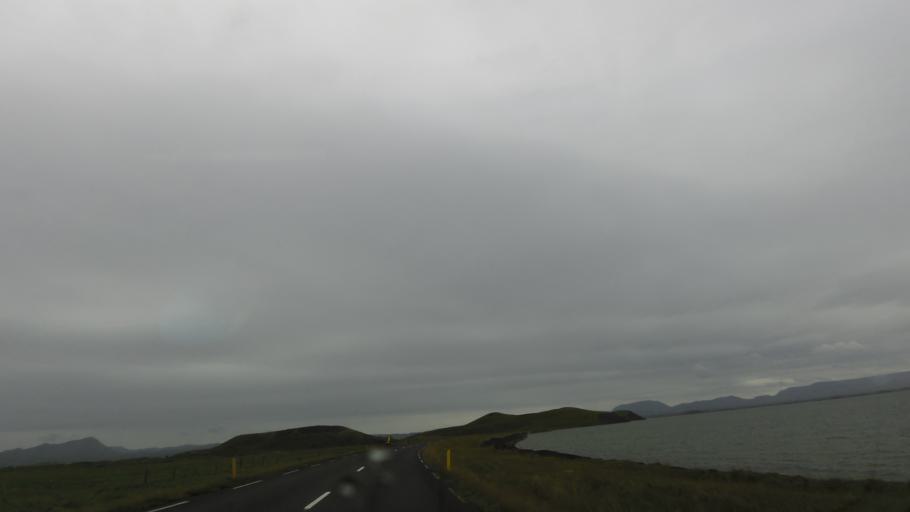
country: IS
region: Northeast
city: Laugar
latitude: 65.6173
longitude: -17.0467
